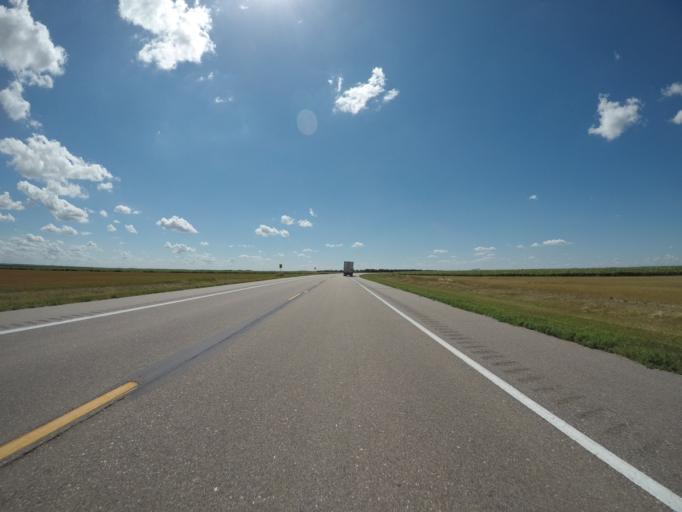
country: US
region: Nebraska
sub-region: Chase County
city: Imperial
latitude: 40.4942
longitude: -101.5926
